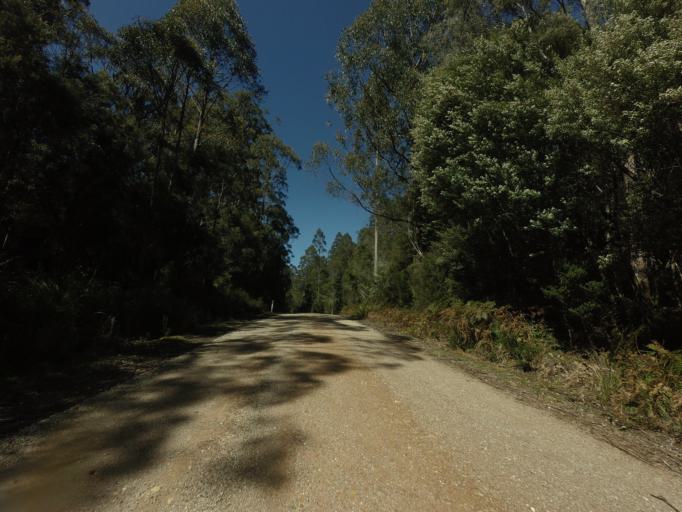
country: AU
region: Tasmania
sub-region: Huon Valley
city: Geeveston
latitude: -42.9884
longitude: 146.3695
